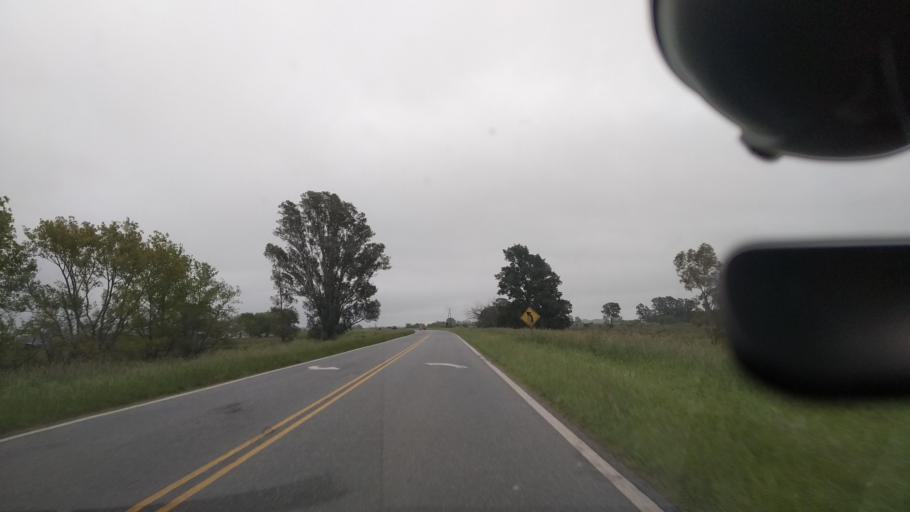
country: AR
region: Buenos Aires
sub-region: Partido de Magdalena
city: Magdalena
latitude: -35.2627
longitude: -57.6310
